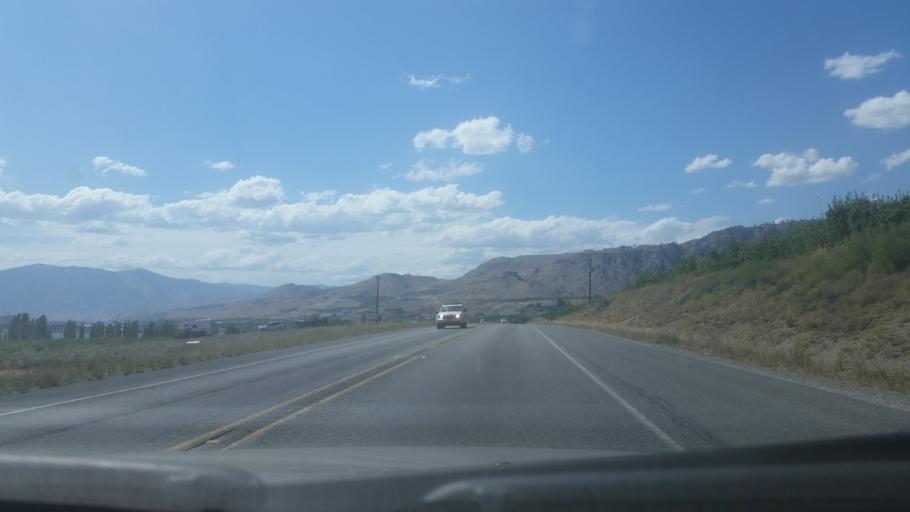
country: US
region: Washington
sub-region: Okanogan County
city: Brewster
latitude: 48.1080
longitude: -119.7422
